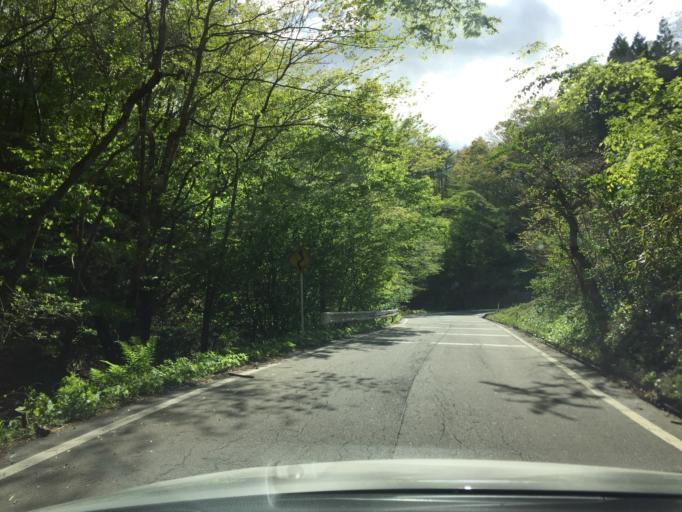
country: JP
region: Miyagi
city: Marumori
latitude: 37.7185
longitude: 140.7832
